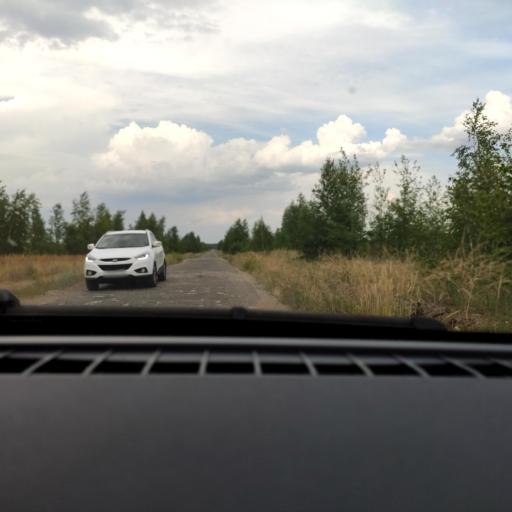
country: RU
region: Voronezj
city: Somovo
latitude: 51.7656
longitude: 39.3185
